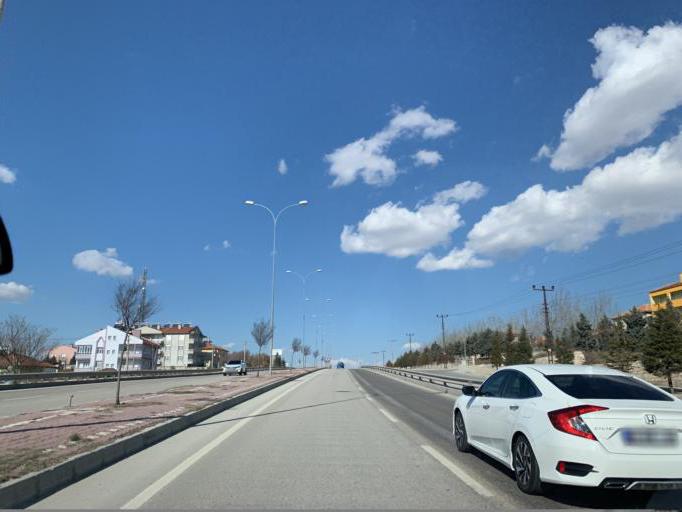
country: TR
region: Konya
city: Cihanbeyli
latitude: 38.6610
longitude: 32.9182
